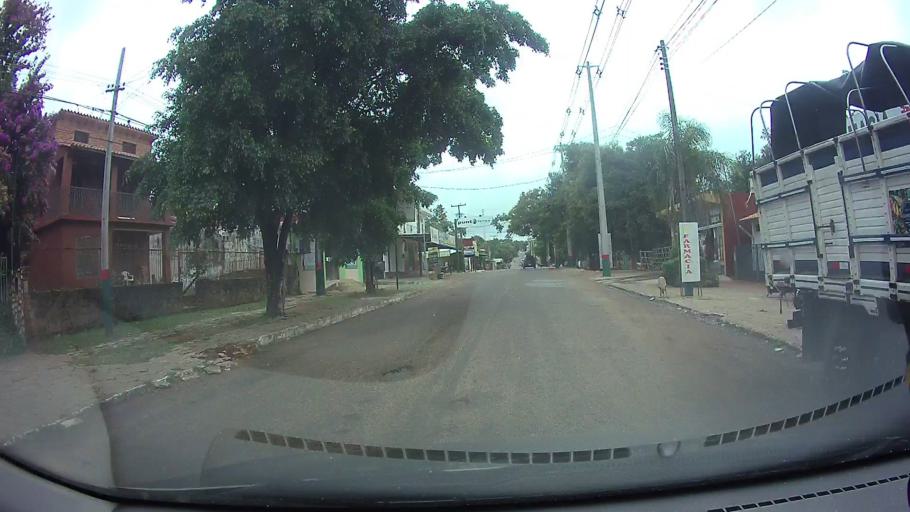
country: PY
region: Cordillera
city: Altos
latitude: -25.2654
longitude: -57.2498
